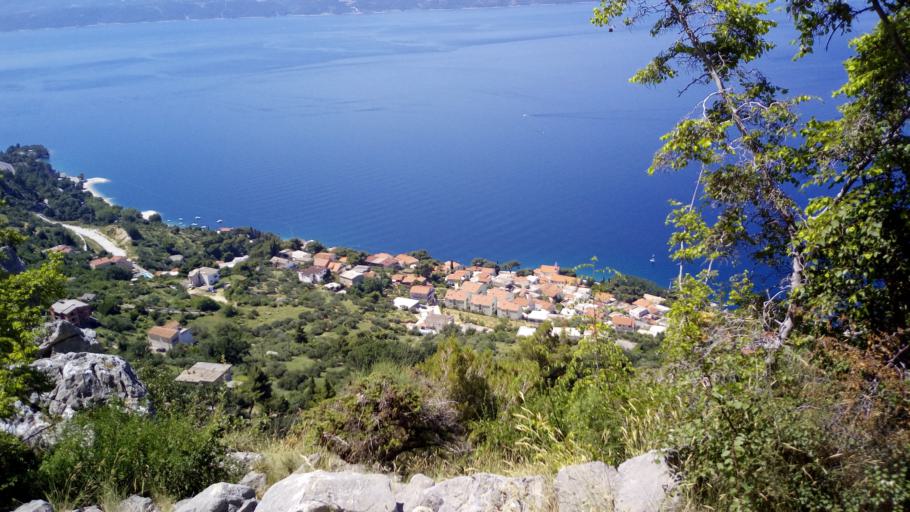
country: HR
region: Splitsko-Dalmatinska
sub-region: Grad Omis
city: Omis
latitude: 43.4439
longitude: 16.7033
